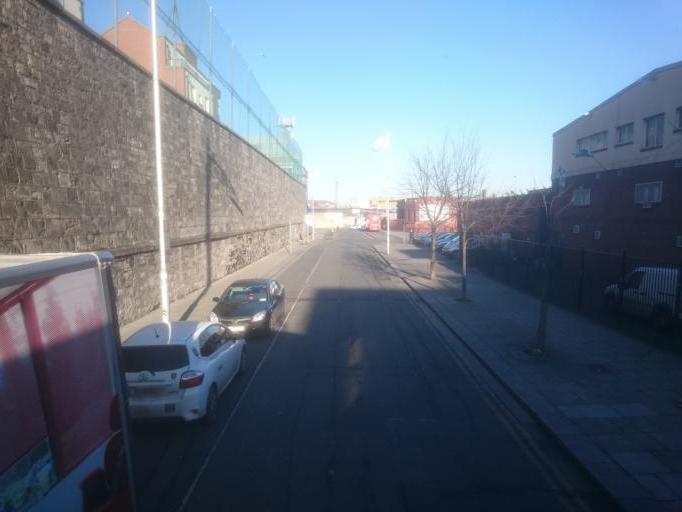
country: IE
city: Fairview
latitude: 53.3504
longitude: -6.2457
